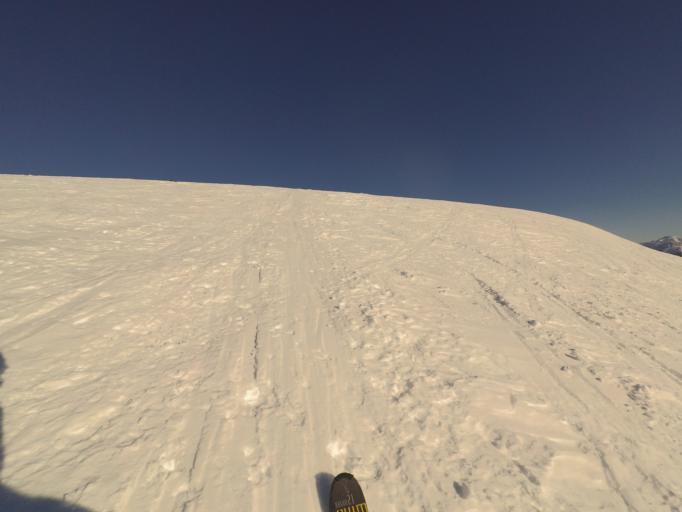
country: AT
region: Salzburg
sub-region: Politischer Bezirk Salzburg-Umgebung
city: Hintersee
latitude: 47.6404
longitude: 13.2725
